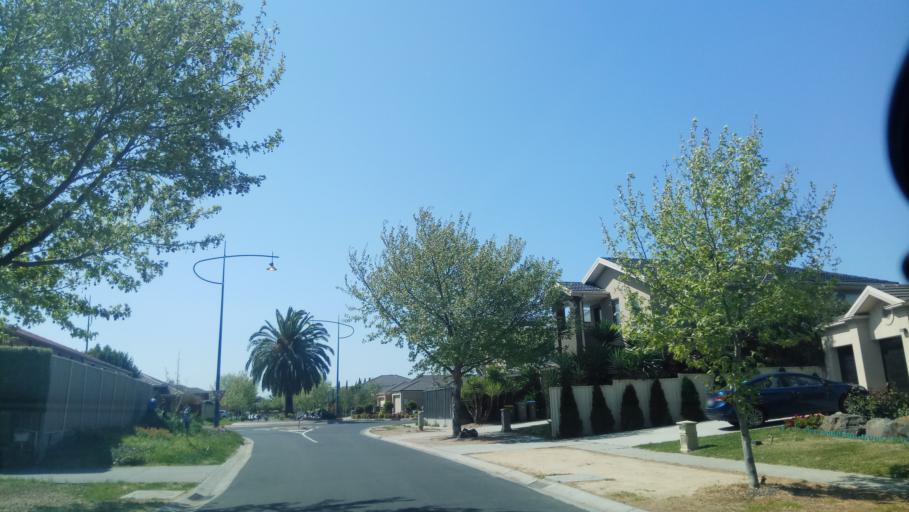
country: AU
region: Victoria
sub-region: Wyndham
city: Point Cook
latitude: -37.8931
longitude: 144.7400
